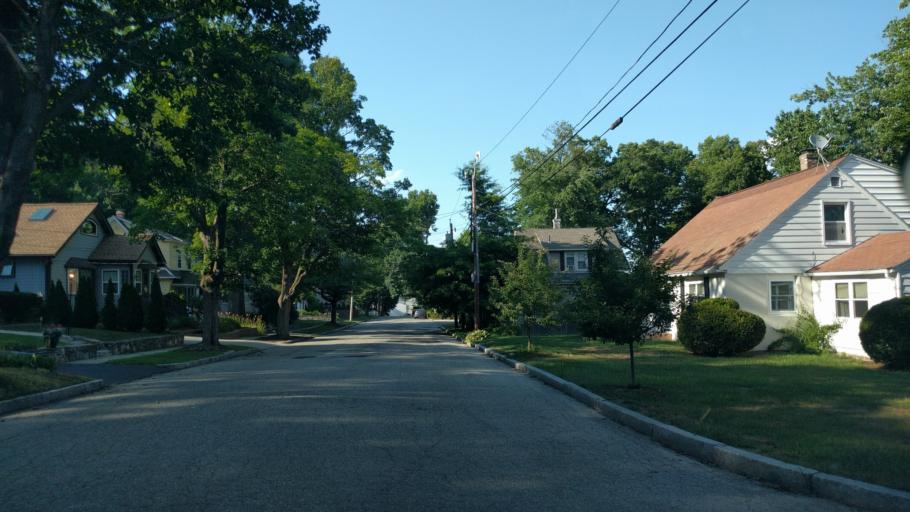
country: US
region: Massachusetts
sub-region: Worcester County
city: Worcester
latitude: 42.2909
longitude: -71.8210
